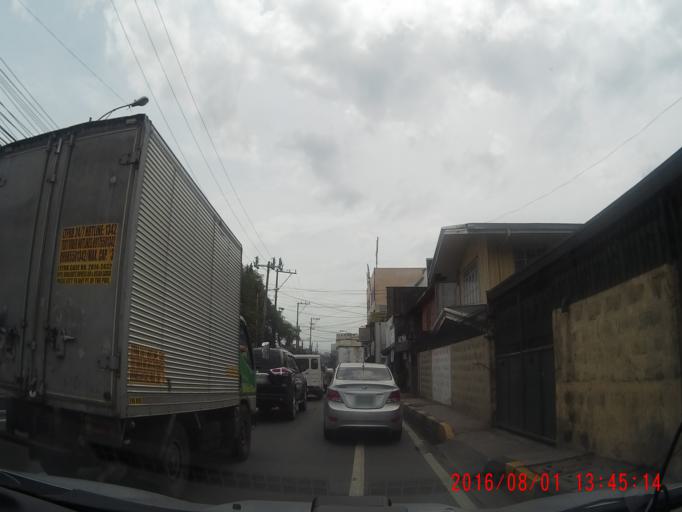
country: PH
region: Metro Manila
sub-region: Pasig
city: Pasig City
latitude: 14.5666
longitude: 121.0788
